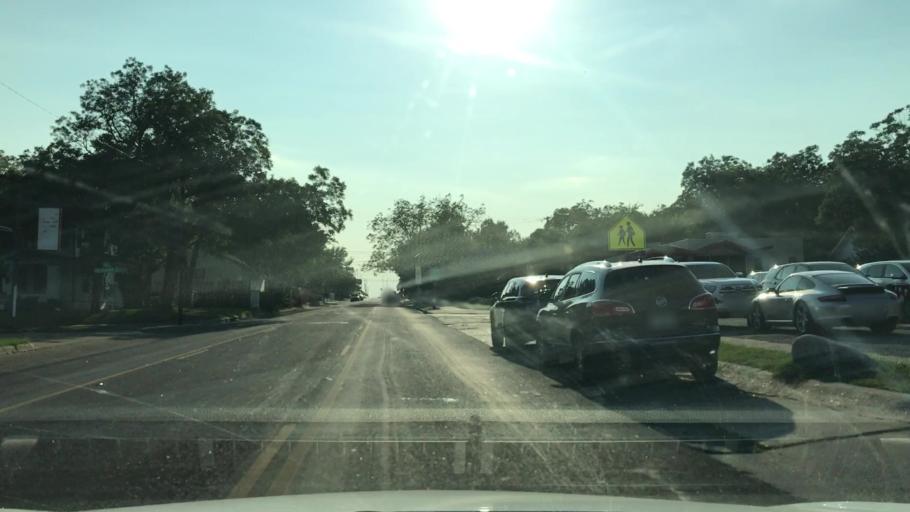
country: US
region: Texas
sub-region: Dallas County
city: Cockrell Hill
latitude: 32.7495
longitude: -96.8448
